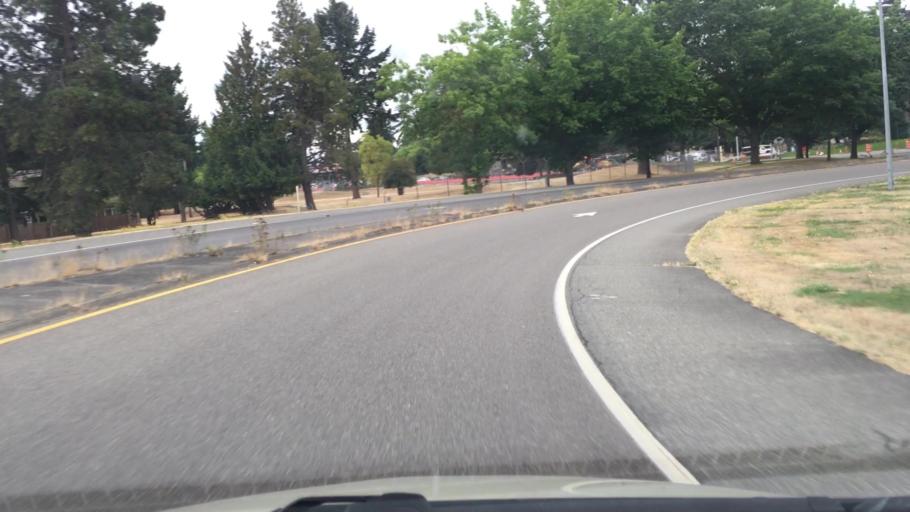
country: US
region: Washington
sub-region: Pierce County
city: Fort Lewis
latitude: 47.1036
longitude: -122.5862
